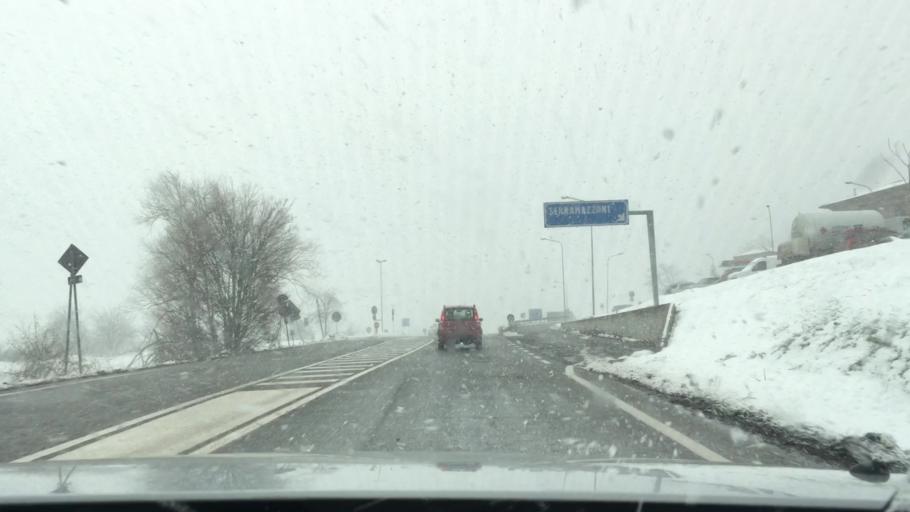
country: IT
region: Emilia-Romagna
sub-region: Provincia di Modena
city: Sant'Antonio
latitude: 44.4082
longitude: 10.8405
